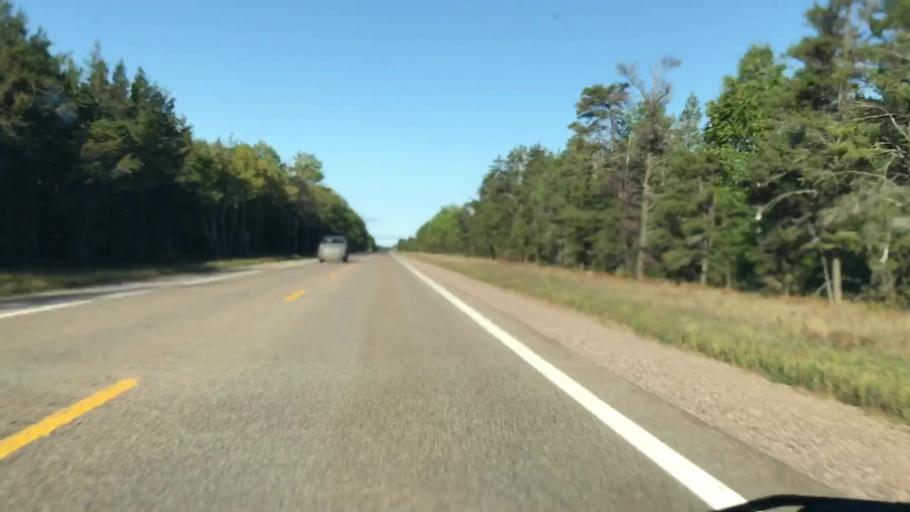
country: US
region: Michigan
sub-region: Mackinac County
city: Saint Ignace
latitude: 46.3585
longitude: -84.8527
